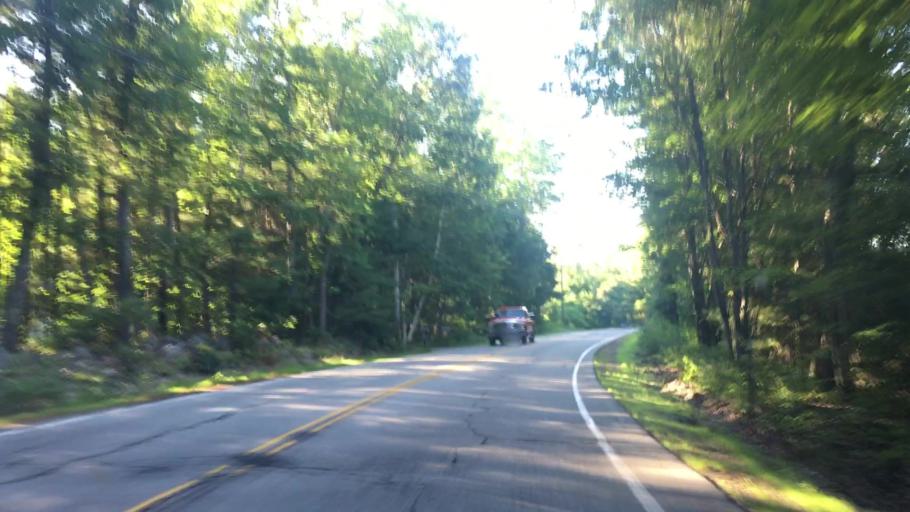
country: US
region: New Hampshire
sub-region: Rockingham County
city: Sandown
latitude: 42.9549
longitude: -71.1983
